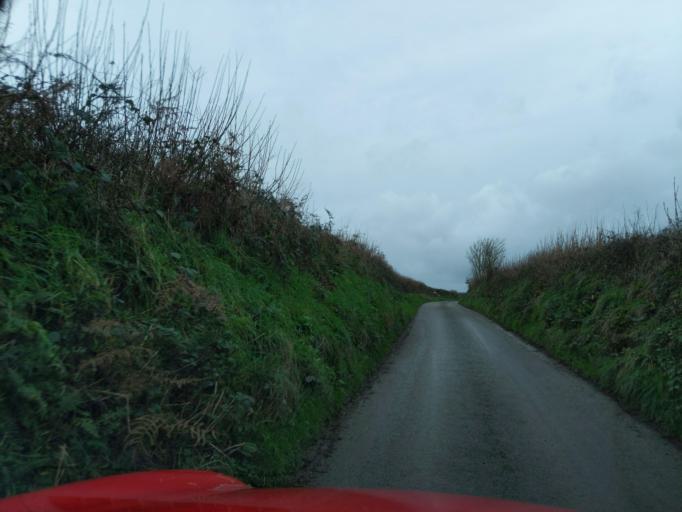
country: GB
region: England
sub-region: Cornwall
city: Duloe
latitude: 50.3458
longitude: -4.5323
